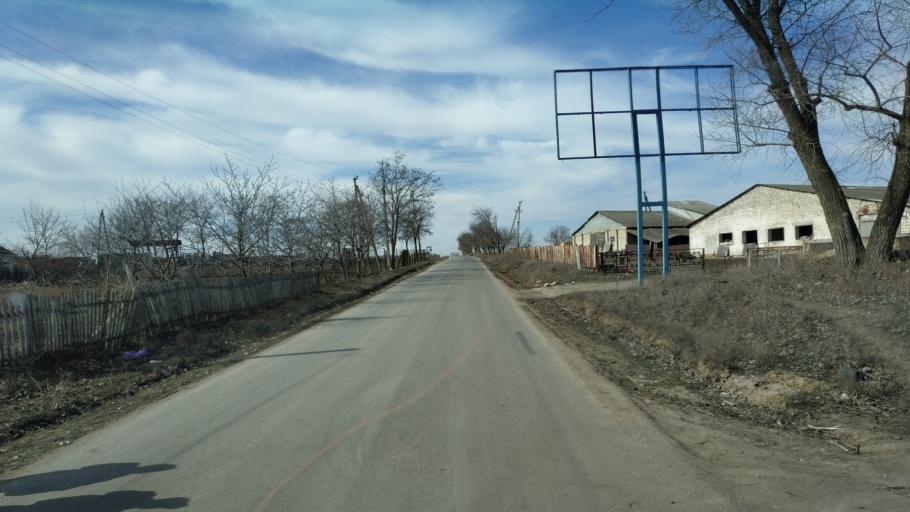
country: MD
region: Nisporeni
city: Nisporeni
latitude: 46.9634
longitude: 28.2085
